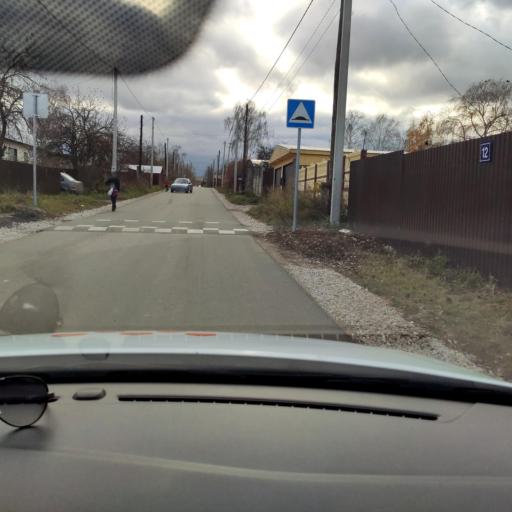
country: RU
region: Tatarstan
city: Stolbishchi
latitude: 55.7398
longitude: 49.2711
